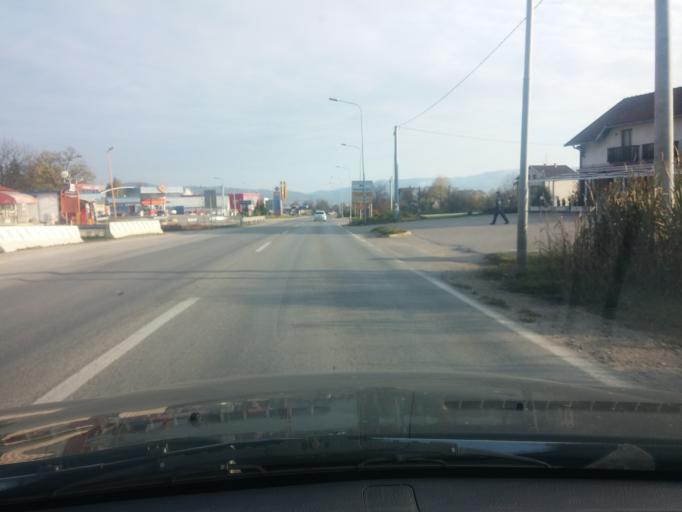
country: BA
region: Republika Srpska
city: Banja Luka
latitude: 44.8279
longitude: 17.1892
